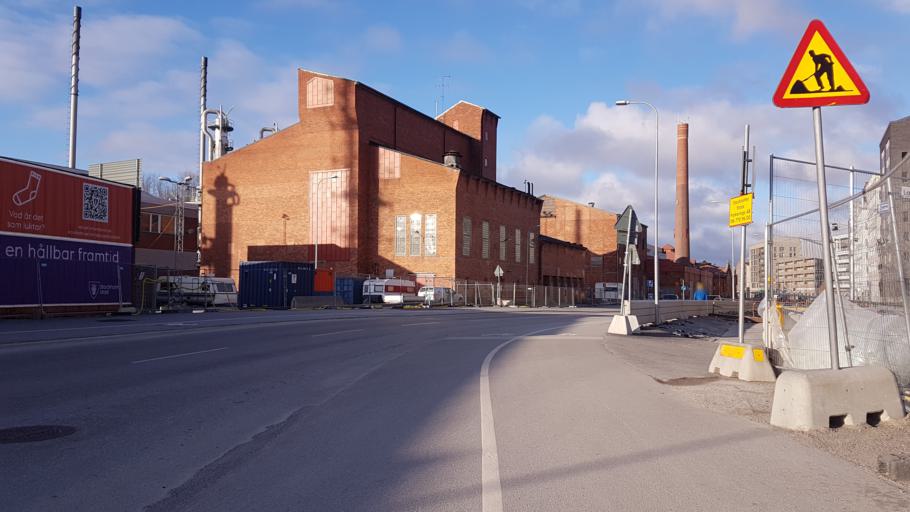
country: SE
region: Stockholm
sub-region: Stockholms Kommun
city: OEstermalm
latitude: 59.3598
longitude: 18.0973
